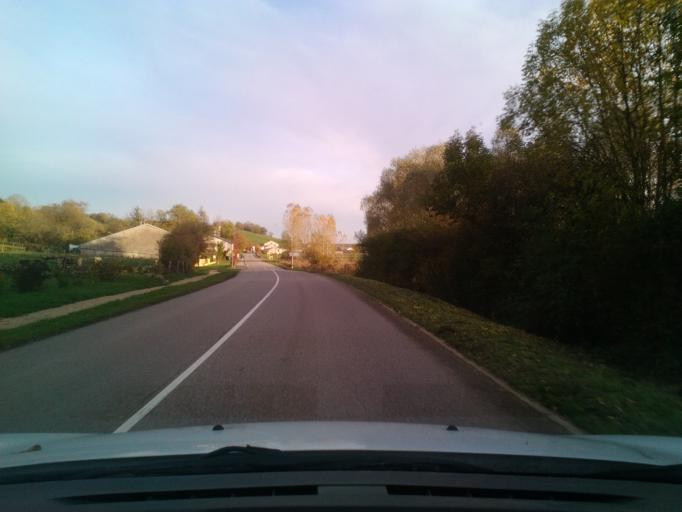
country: FR
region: Lorraine
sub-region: Departement des Vosges
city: Mirecourt
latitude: 48.2645
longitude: 6.1663
